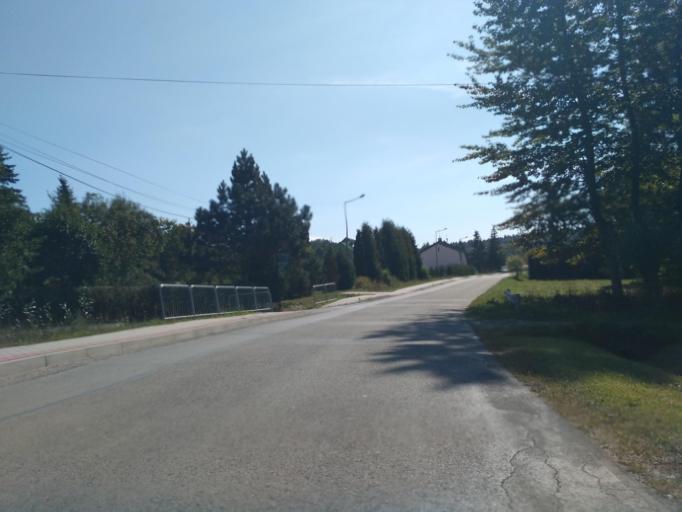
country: PL
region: Subcarpathian Voivodeship
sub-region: Powiat brzozowski
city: Niebocko
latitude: 49.6564
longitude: 22.1369
